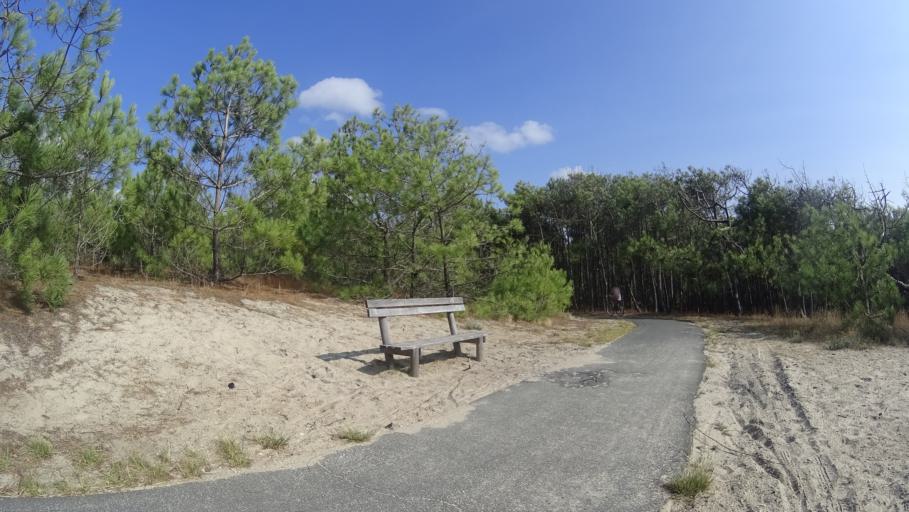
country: FR
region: Aquitaine
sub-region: Departement de la Gironde
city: Lacanau
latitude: 44.9795
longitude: -1.2016
